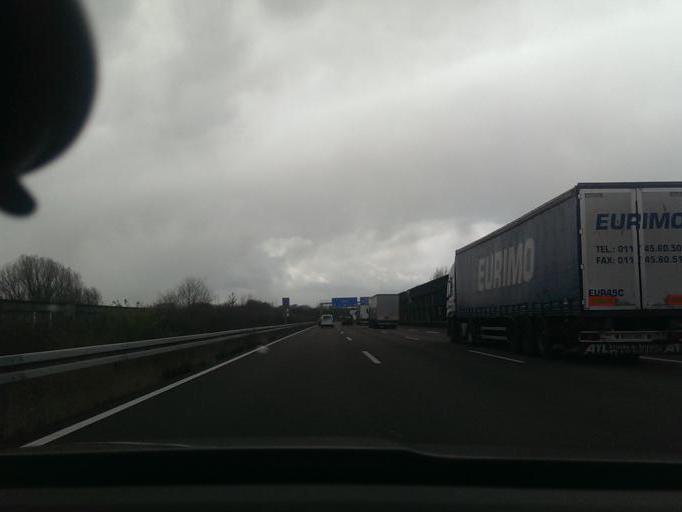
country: DE
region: Lower Saxony
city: Braunschweig
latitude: 52.3134
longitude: 10.5323
